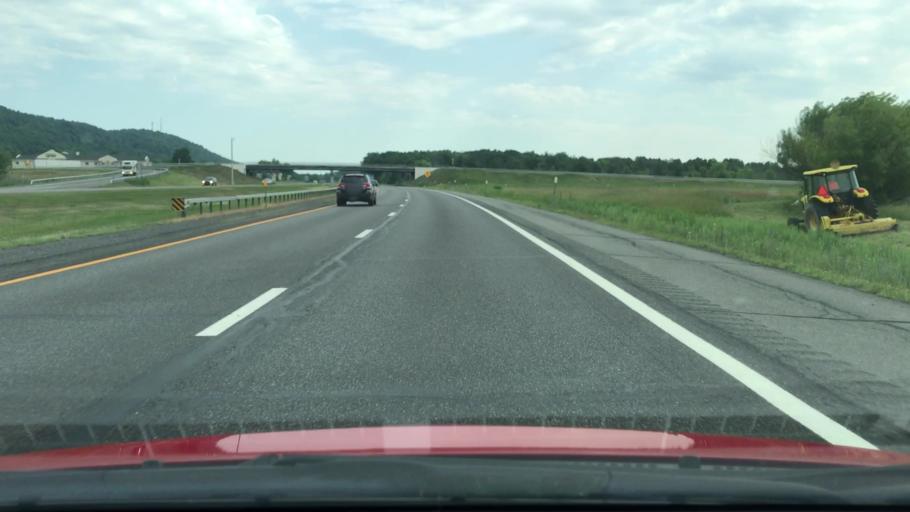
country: US
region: New York
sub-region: Greene County
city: Coxsackie
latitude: 42.3909
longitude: -73.8256
